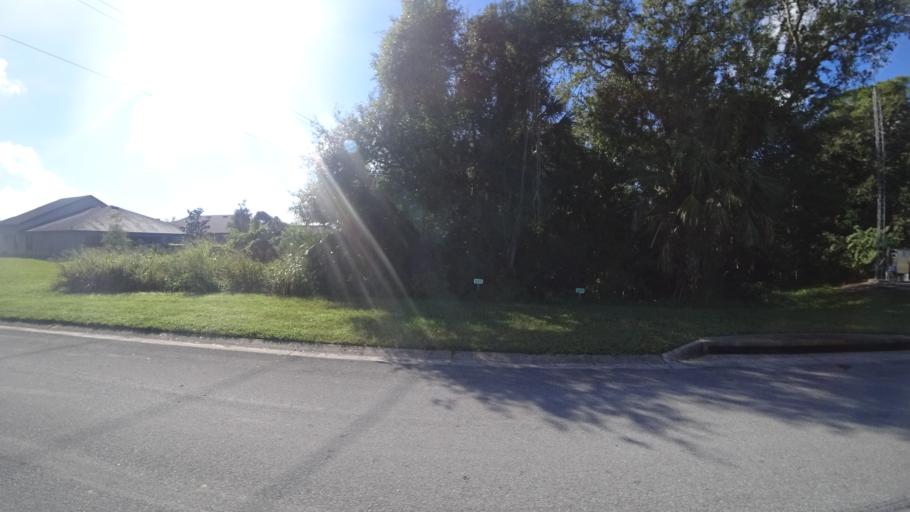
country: US
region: Florida
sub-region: Manatee County
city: Ellenton
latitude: 27.5905
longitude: -82.4985
